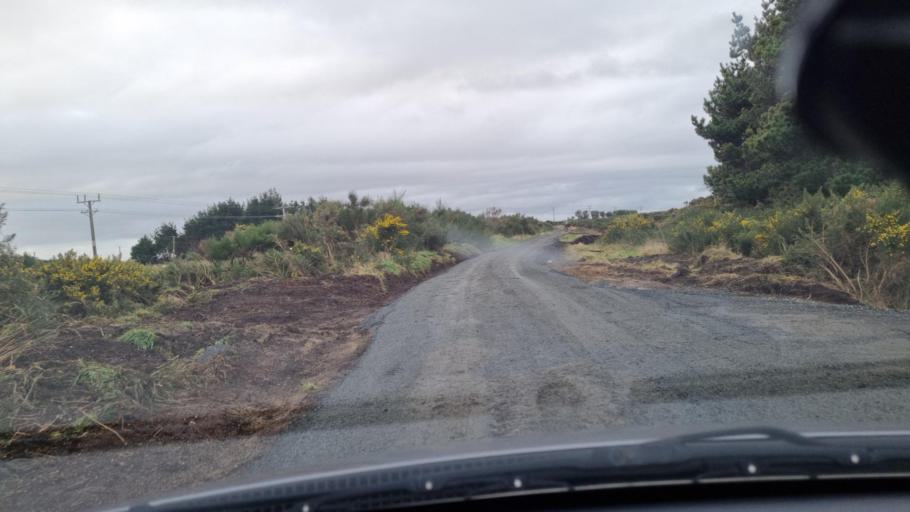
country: NZ
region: Southland
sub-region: Invercargill City
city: Bluff
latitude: -46.5411
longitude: 168.3026
